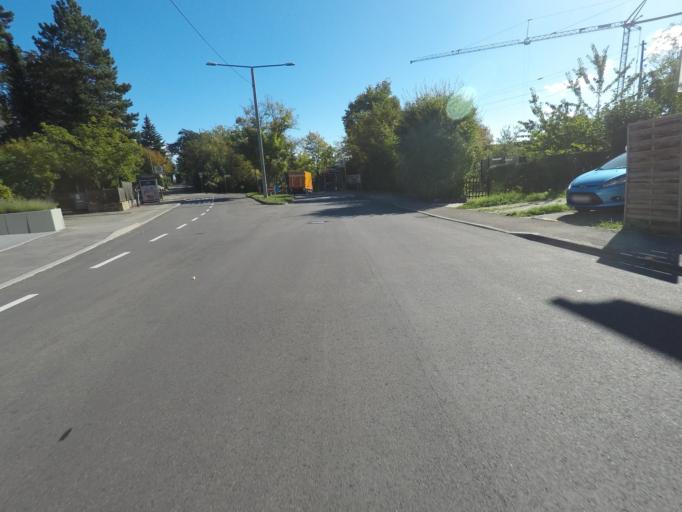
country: DE
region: Baden-Wuerttemberg
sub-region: Regierungsbezirk Stuttgart
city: Stuttgart
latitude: 48.7477
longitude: 9.1207
